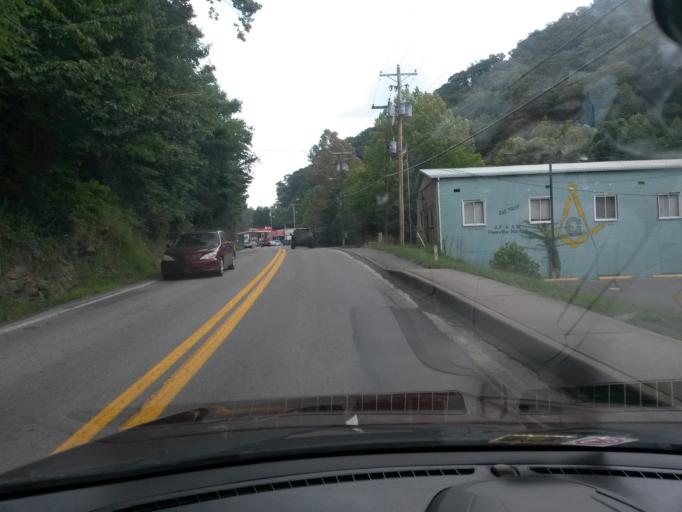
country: US
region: West Virginia
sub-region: Wyoming County
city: Pineville
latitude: 37.5849
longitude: -81.5344
